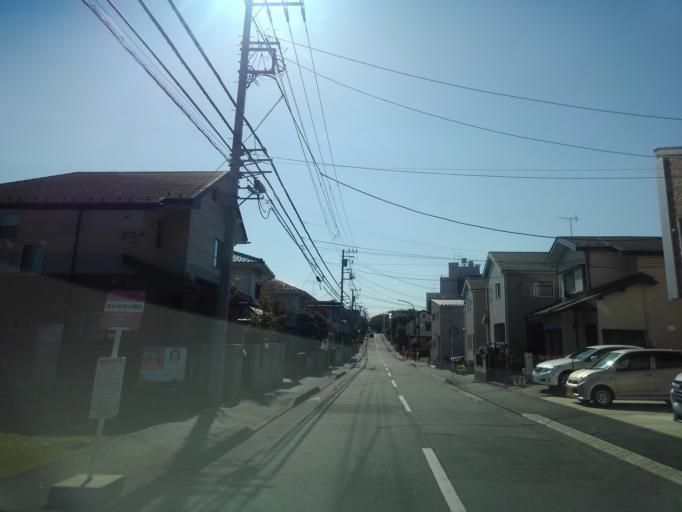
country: JP
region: Tokyo
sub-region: Machida-shi
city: Machida
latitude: 35.5790
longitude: 139.3986
